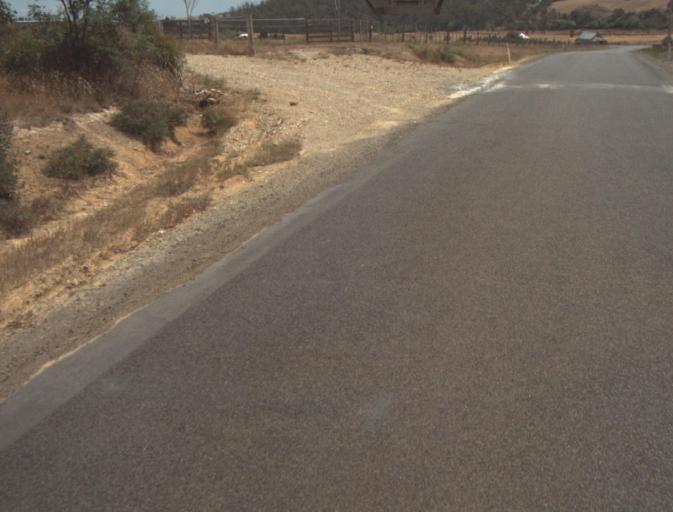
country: AU
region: Tasmania
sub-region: Launceston
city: Mayfield
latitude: -41.2292
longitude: 147.1445
